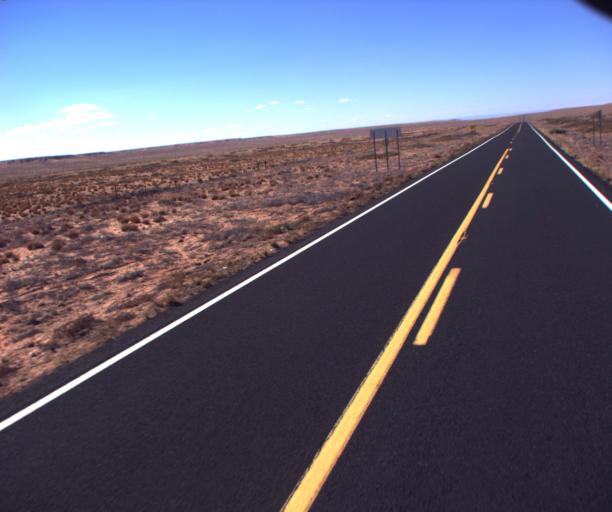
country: US
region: Arizona
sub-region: Coconino County
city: Tuba City
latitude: 36.0228
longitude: -111.1375
